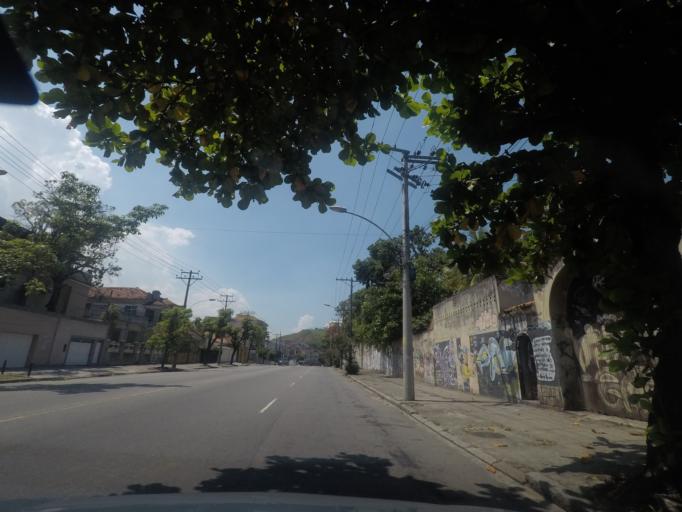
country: BR
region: Rio de Janeiro
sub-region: Rio De Janeiro
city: Rio de Janeiro
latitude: -22.8752
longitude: -43.2573
